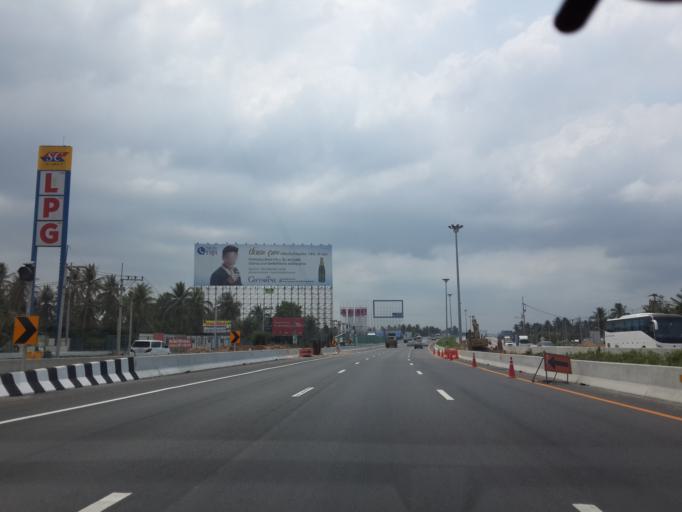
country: TH
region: Chon Buri
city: Ban Talat Bueng
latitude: 13.0115
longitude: 100.9963
